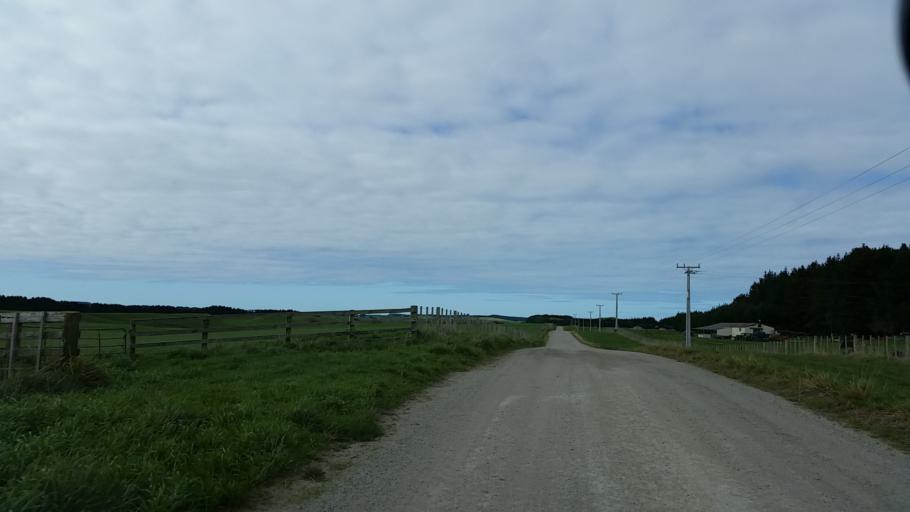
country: NZ
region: Taranaki
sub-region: South Taranaki District
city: Patea
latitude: -39.8040
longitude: 174.6927
